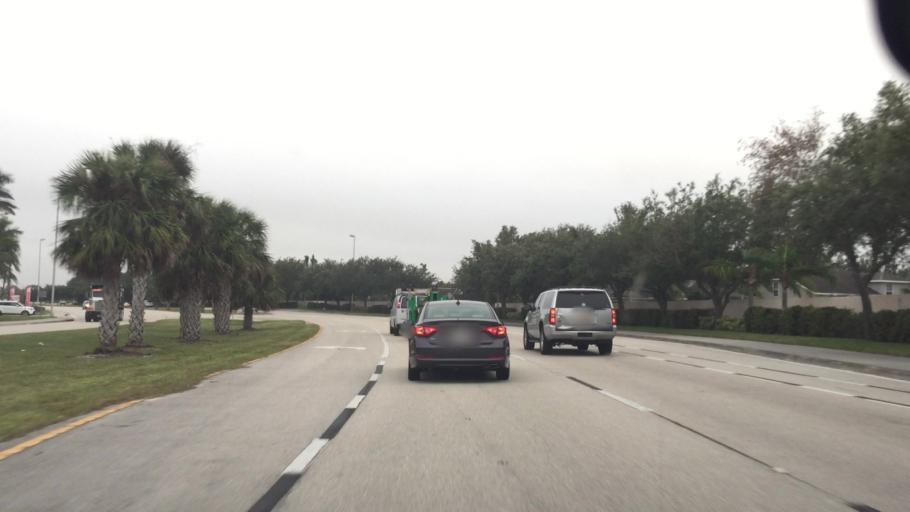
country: US
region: Florida
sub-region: Lee County
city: Three Oaks
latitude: 26.4823
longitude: -81.7986
